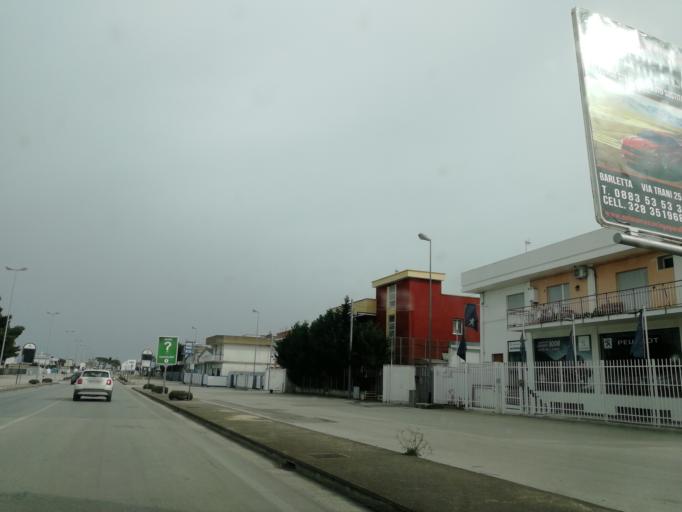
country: IT
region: Apulia
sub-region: Provincia di Barletta - Andria - Trani
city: Barletta
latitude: 41.3102
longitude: 16.3095
